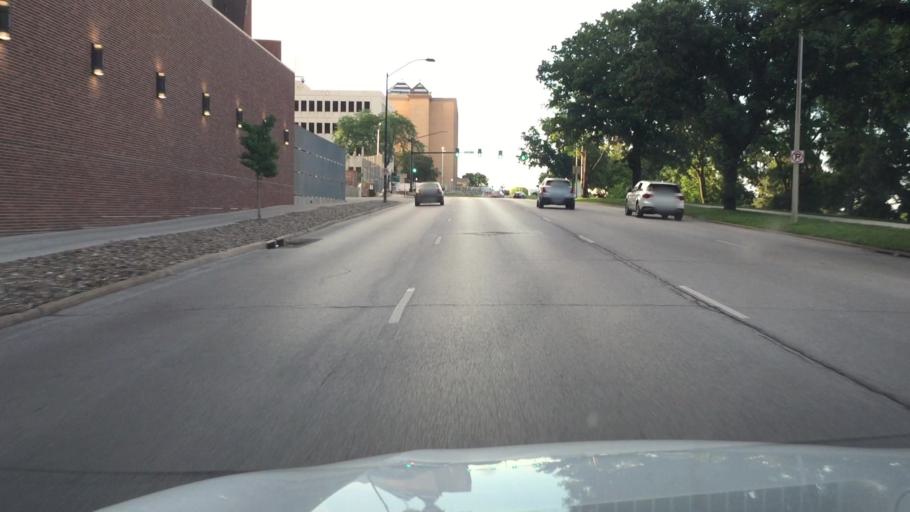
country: US
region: Iowa
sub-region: Polk County
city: Des Moines
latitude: 41.5923
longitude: -93.6204
